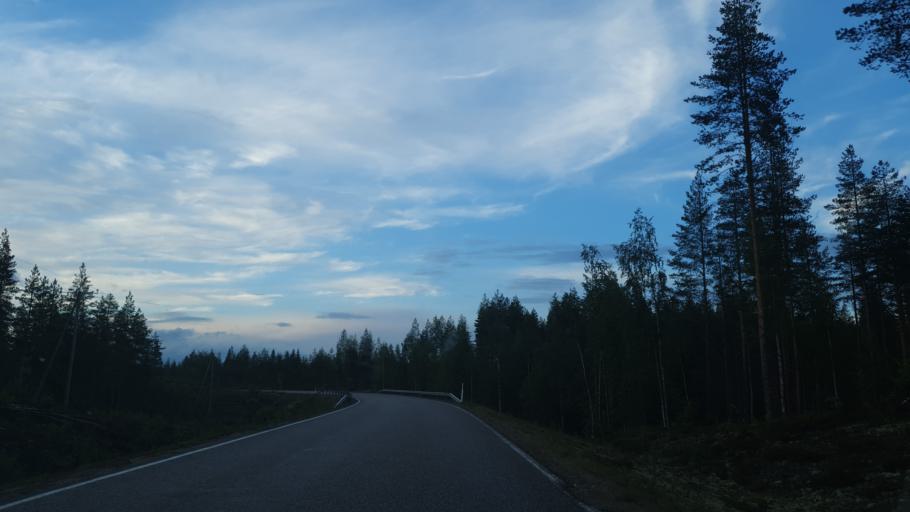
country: FI
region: Kainuu
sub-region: Kehys-Kainuu
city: Kuhmo
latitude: 63.8640
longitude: 29.8426
